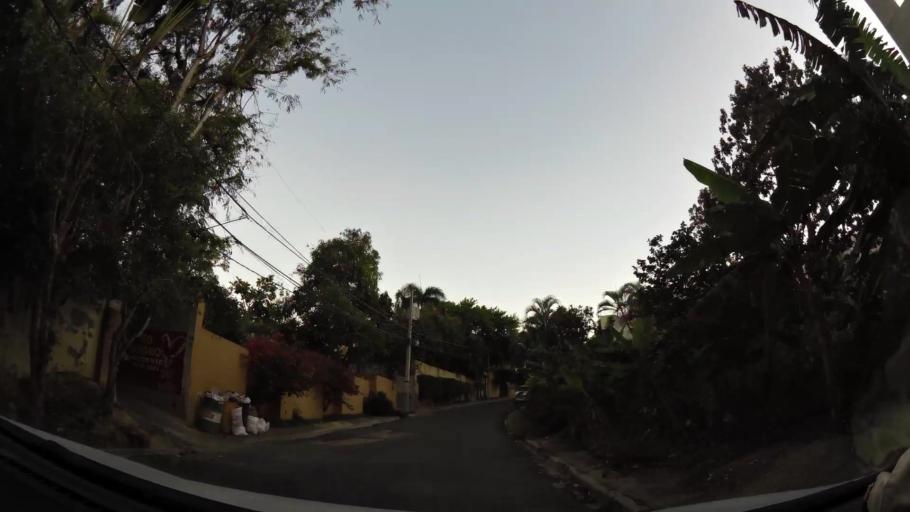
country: DO
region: Nacional
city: La Agustina
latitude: 18.5045
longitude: -69.9518
